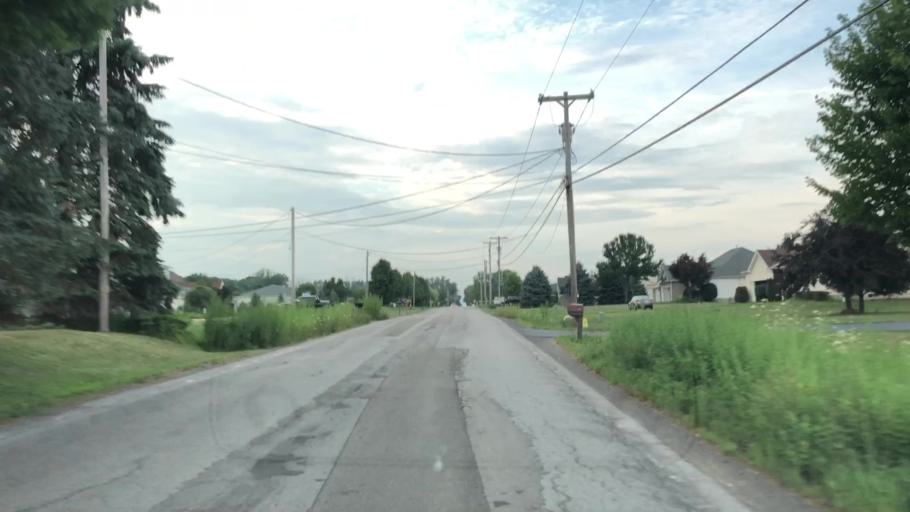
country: US
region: New York
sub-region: Erie County
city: Billington Heights
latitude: 42.8004
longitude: -78.6059
